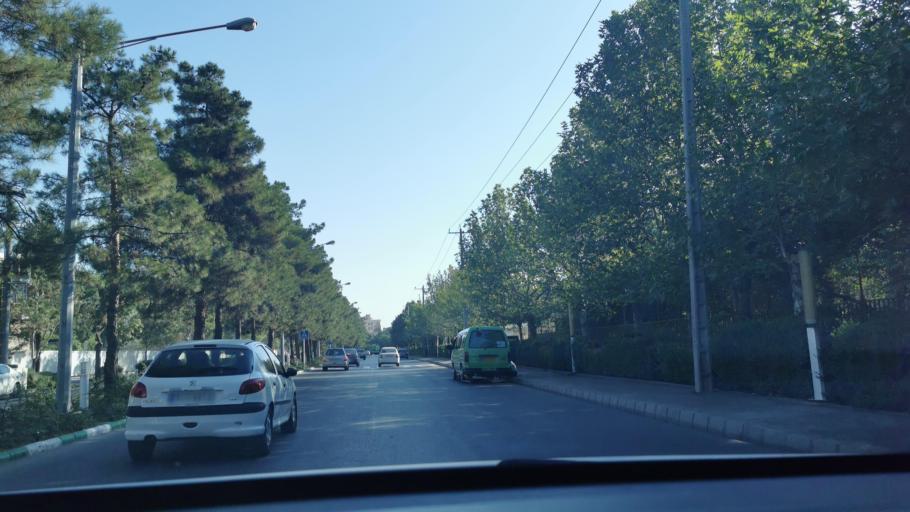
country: IR
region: Razavi Khorasan
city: Mashhad
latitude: 36.3167
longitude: 59.5265
